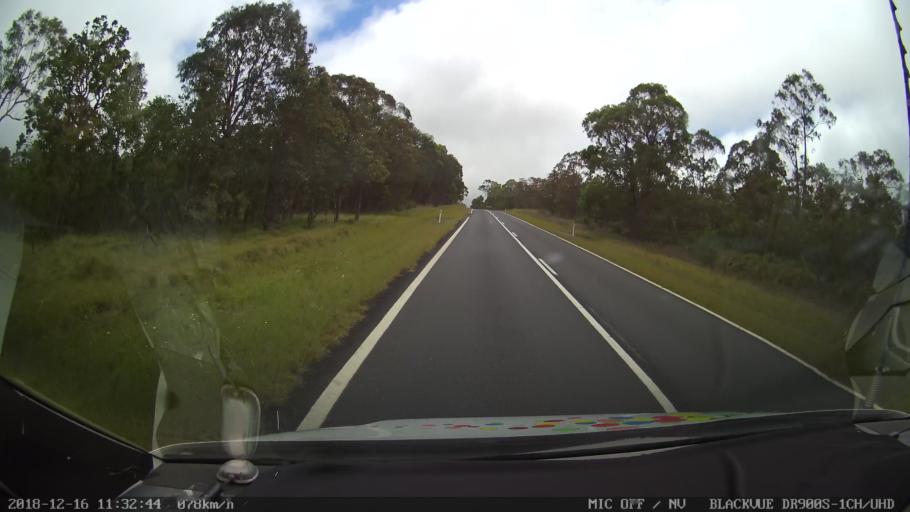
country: AU
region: New South Wales
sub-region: Tenterfield Municipality
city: Carrolls Creek
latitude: -29.0126
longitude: 152.1385
